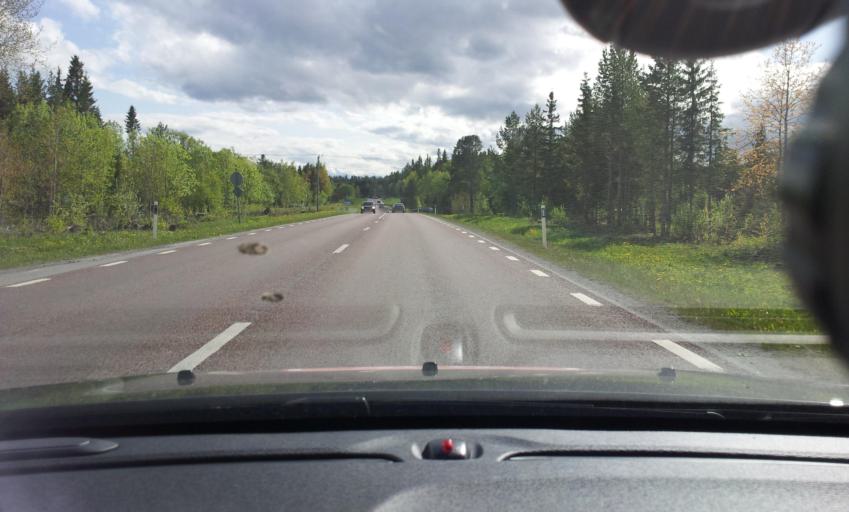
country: SE
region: Jaemtland
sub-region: OEstersunds Kommun
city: Brunflo
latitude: 63.0530
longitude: 14.8278
